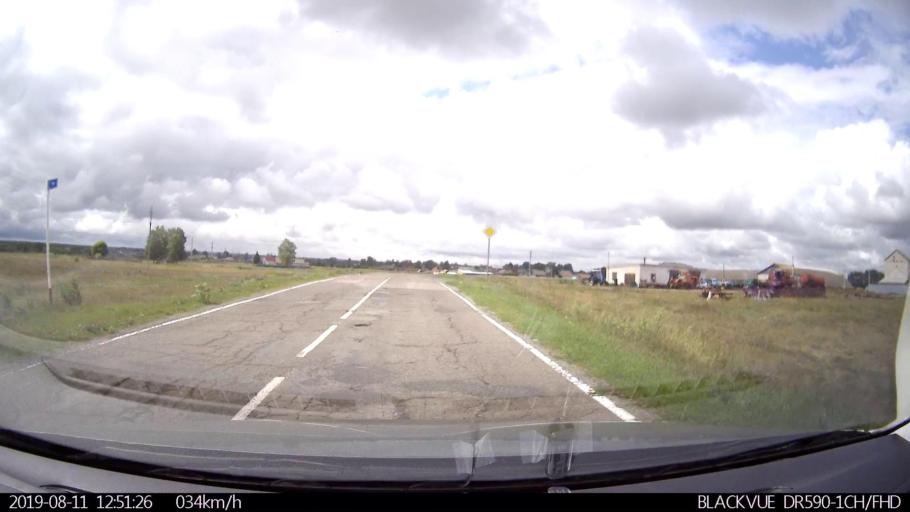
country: RU
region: Ulyanovsk
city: Ignatovka
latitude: 53.8757
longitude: 47.6626
